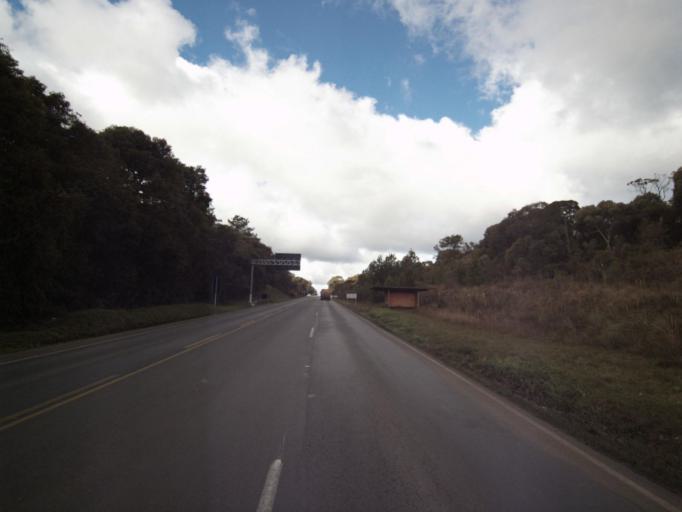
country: BR
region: Santa Catarina
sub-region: Concordia
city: Concordia
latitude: -26.9710
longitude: -51.8505
